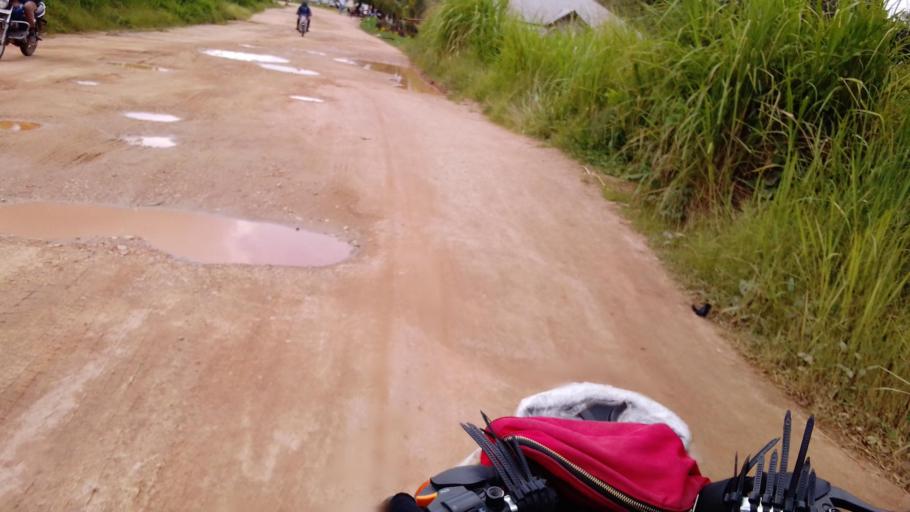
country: SL
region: Eastern Province
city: Koidu
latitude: 8.6732
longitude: -10.9803
